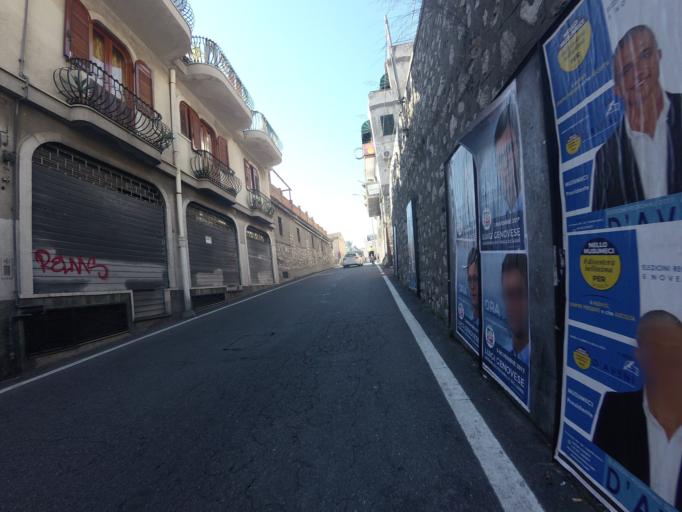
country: IT
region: Sicily
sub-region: Messina
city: Taormina
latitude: 37.8542
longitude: 15.2879
